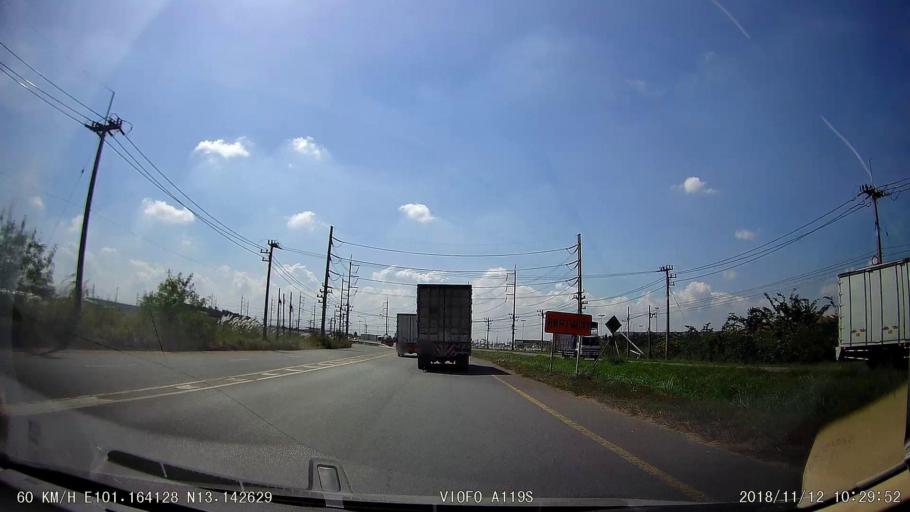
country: TH
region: Rayong
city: Pluak Daeng
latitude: 13.1334
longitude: 101.1666
